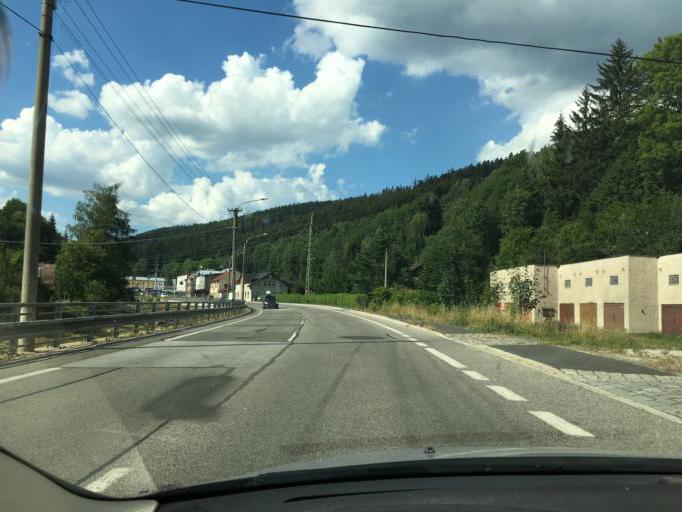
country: CZ
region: Kralovehradecky
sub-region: Okres Trutnov
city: Vrchlabi
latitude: 50.6508
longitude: 15.6052
